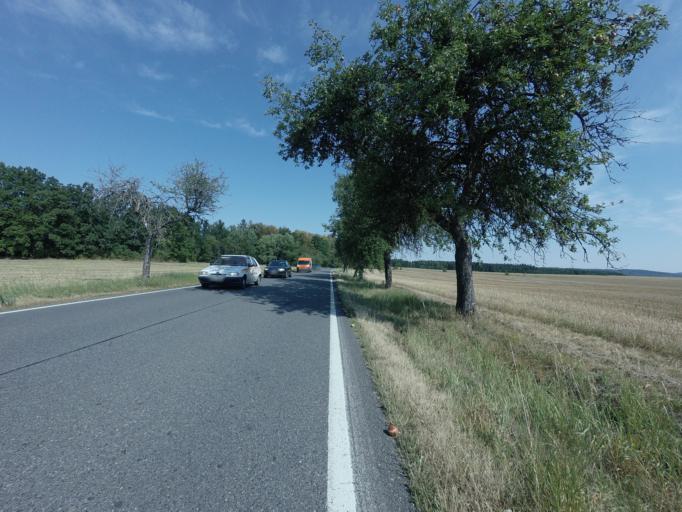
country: CZ
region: Jihocesky
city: Milevsko
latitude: 49.4157
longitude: 14.3583
